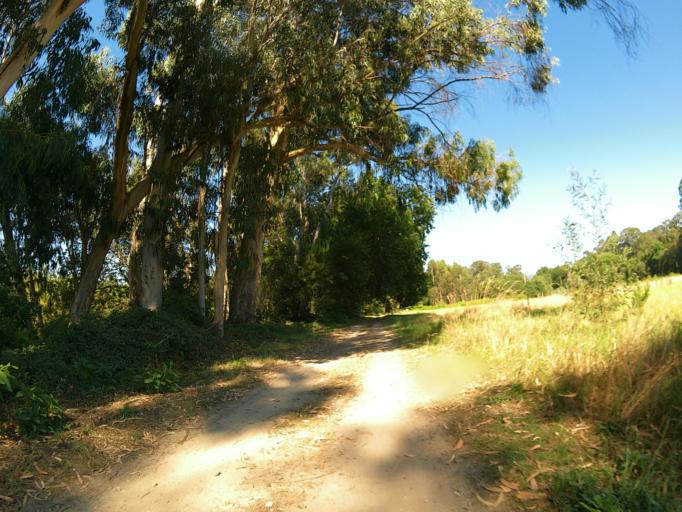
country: PT
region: Viana do Castelo
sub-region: Ponte de Lima
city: Ponte de Lima
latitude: 41.7612
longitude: -8.6139
